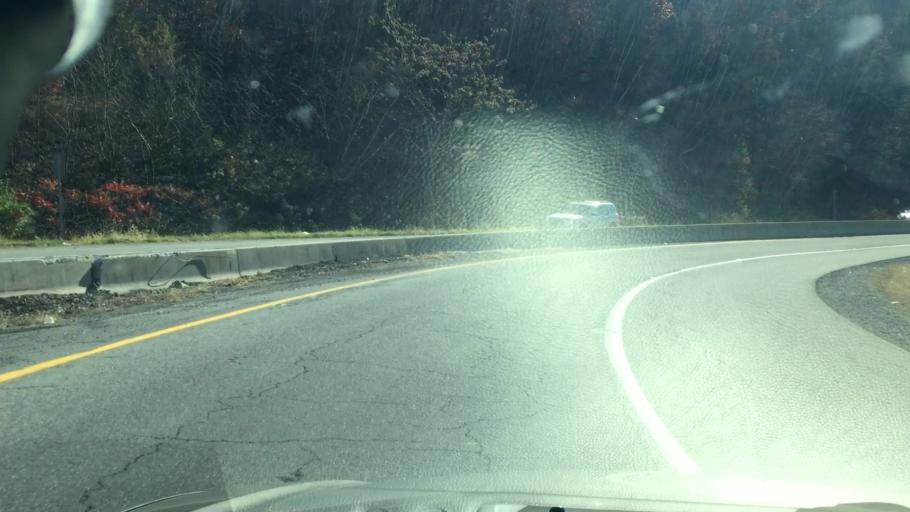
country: US
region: Pennsylvania
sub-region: Luzerne County
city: Ashley
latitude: 41.2032
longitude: -75.9017
